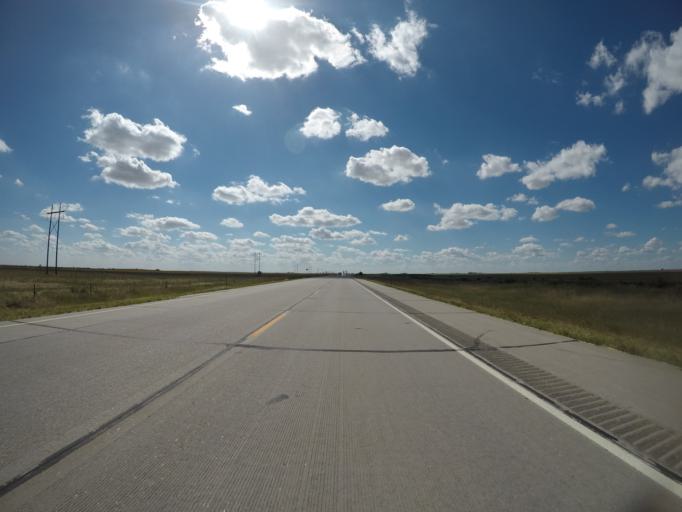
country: US
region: Colorado
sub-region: Phillips County
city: Holyoke
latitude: 40.6031
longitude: -102.4157
